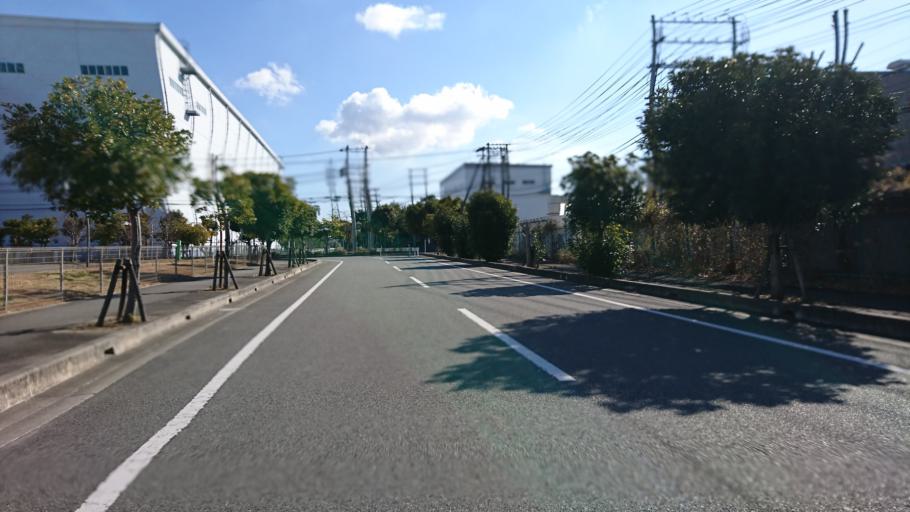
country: JP
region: Hyogo
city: Kakogawacho-honmachi
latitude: 34.7510
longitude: 134.7839
